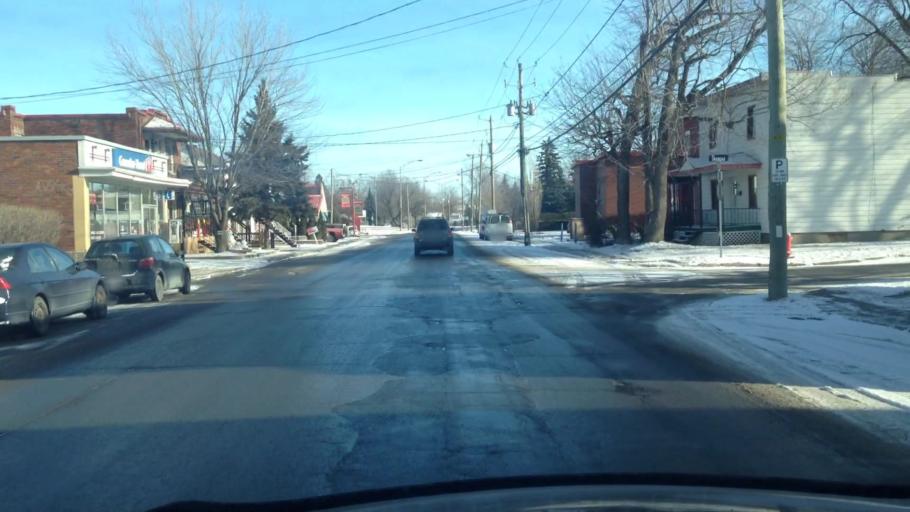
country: CA
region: Quebec
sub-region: Monteregie
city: Beauharnois
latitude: 45.3157
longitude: -73.8699
